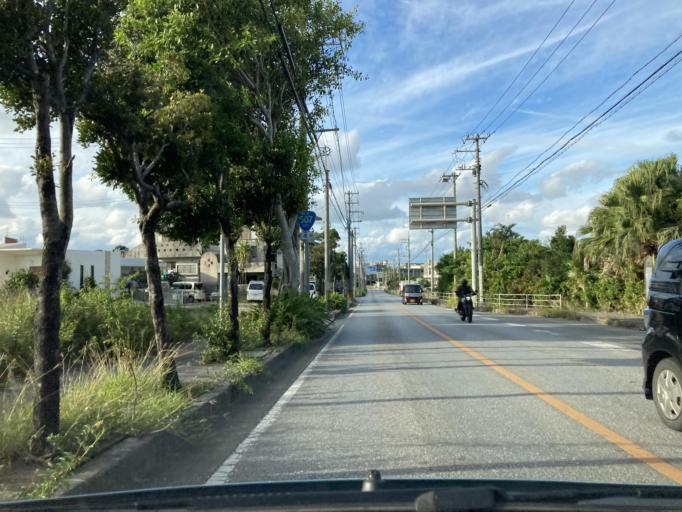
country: JP
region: Okinawa
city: Tomigusuku
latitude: 26.1481
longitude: 127.7247
